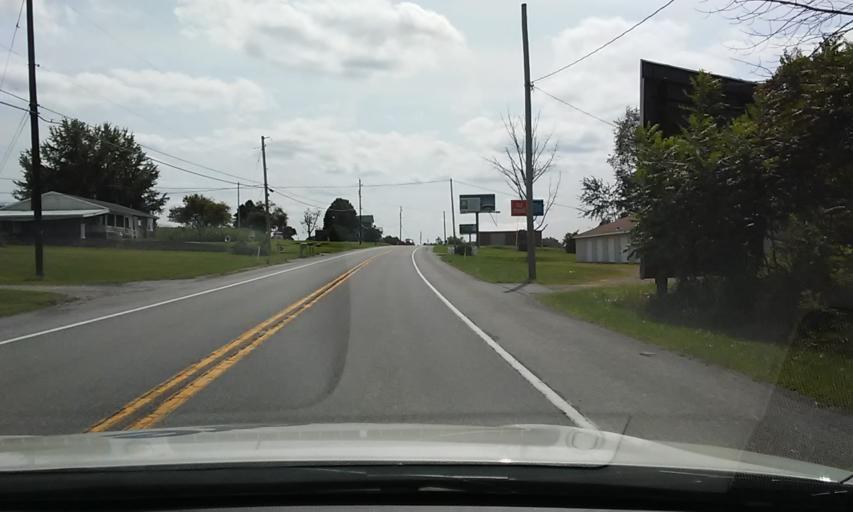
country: US
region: Pennsylvania
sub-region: Jefferson County
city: Punxsutawney
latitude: 40.8623
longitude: -79.0211
